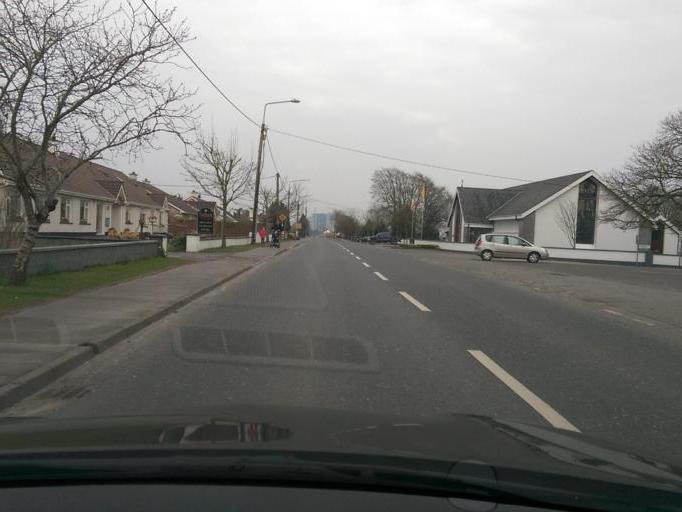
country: IE
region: Leinster
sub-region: An Longfort
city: Lanesborough
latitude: 53.6762
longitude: -8.0056
